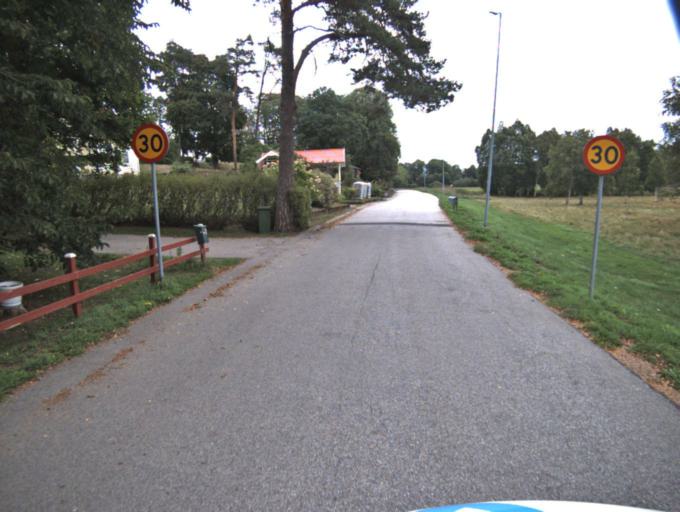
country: SE
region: Vaestra Goetaland
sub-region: Ulricehamns Kommun
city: Ulricehamn
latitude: 57.8423
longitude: 13.2833
